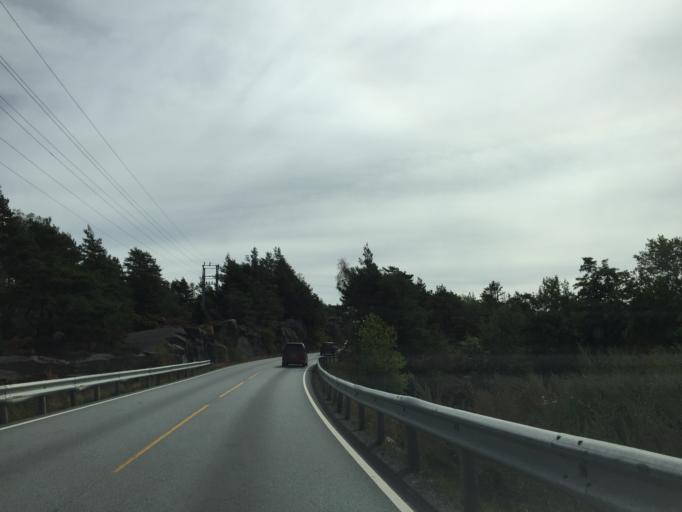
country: NO
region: Ostfold
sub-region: Fredrikstad
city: Fredrikstad
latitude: 59.0969
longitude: 10.9213
